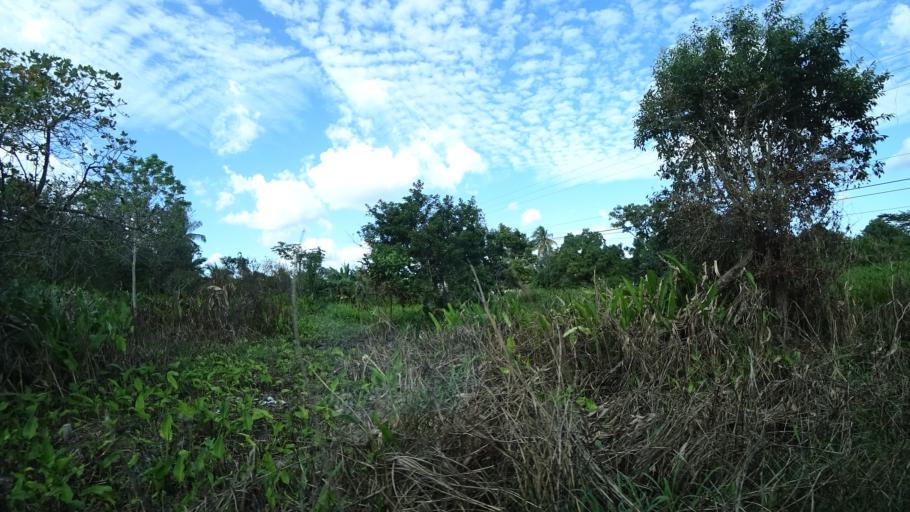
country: BZ
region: Belize
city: Belize City
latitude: 17.5647
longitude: -88.4065
